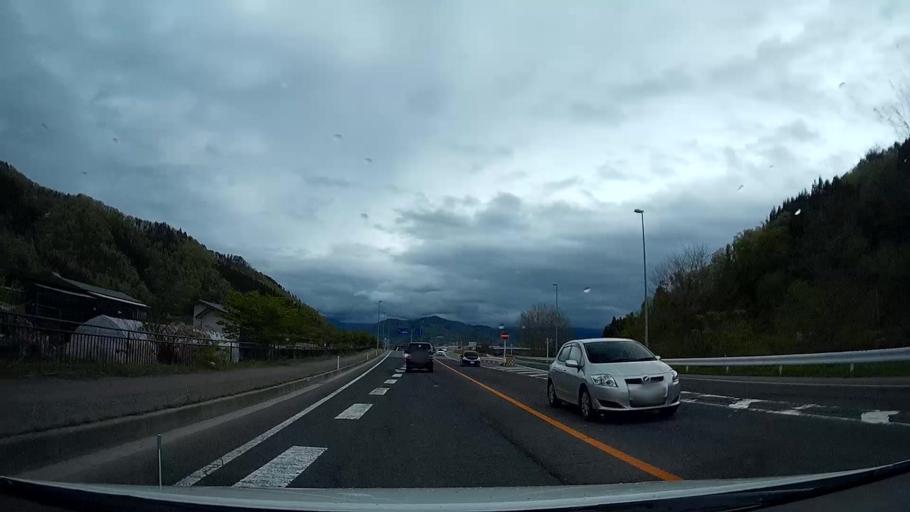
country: JP
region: Yamagata
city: Kaminoyama
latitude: 38.1304
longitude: 140.2431
